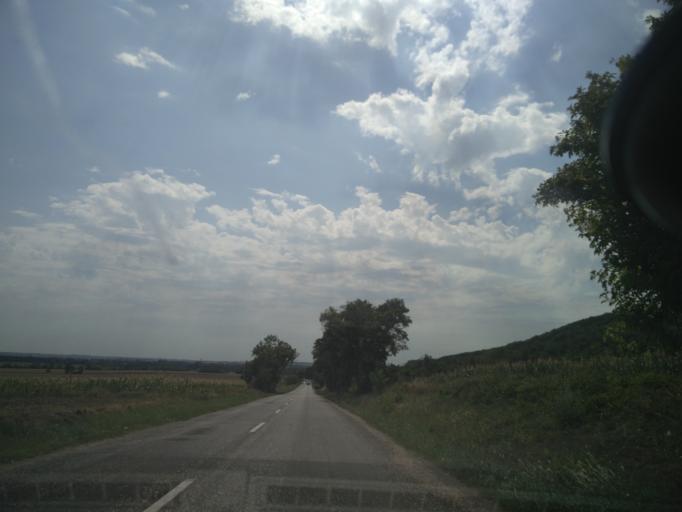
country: HU
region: Fejer
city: Velence
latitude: 47.2553
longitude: 18.6242
